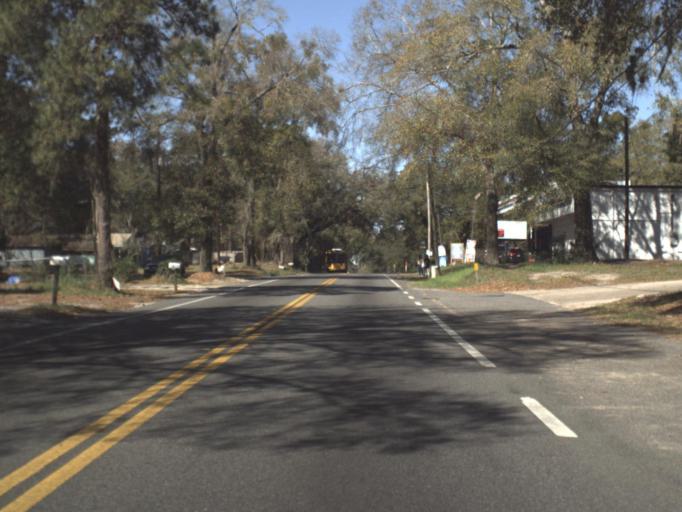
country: US
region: Florida
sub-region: Leon County
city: Tallahassee
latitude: 30.4127
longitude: -84.3071
